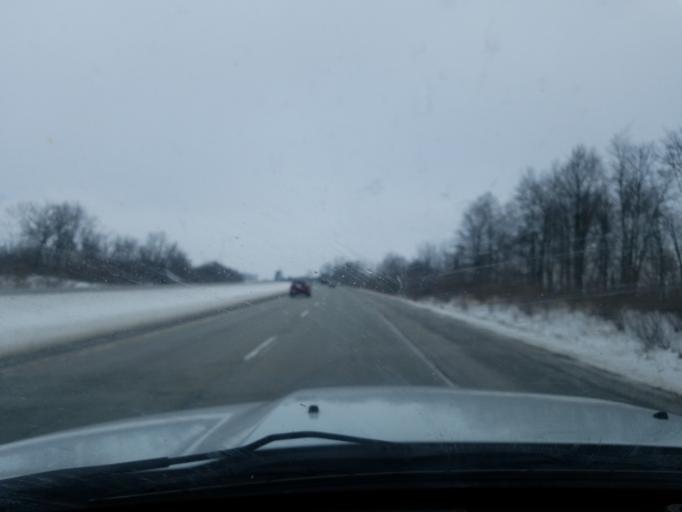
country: US
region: Indiana
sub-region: Marshall County
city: Argos
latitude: 41.1648
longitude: -86.2396
